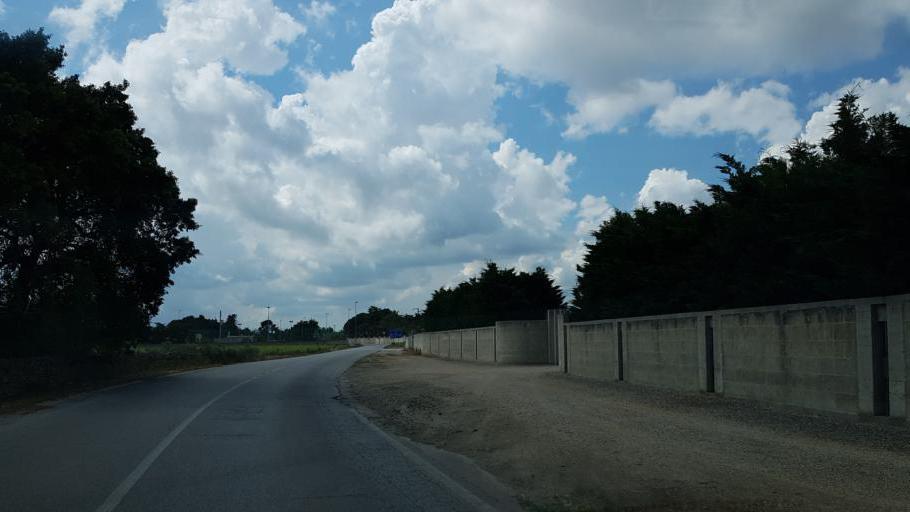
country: IT
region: Apulia
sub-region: Provincia di Brindisi
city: Mesagne
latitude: 40.5455
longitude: 17.8149
